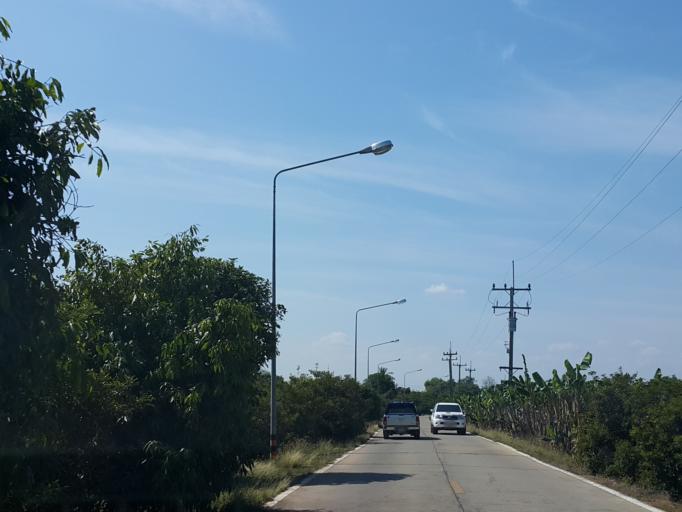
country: TH
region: Sukhothai
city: Si Samrong
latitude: 17.2213
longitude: 99.8531
